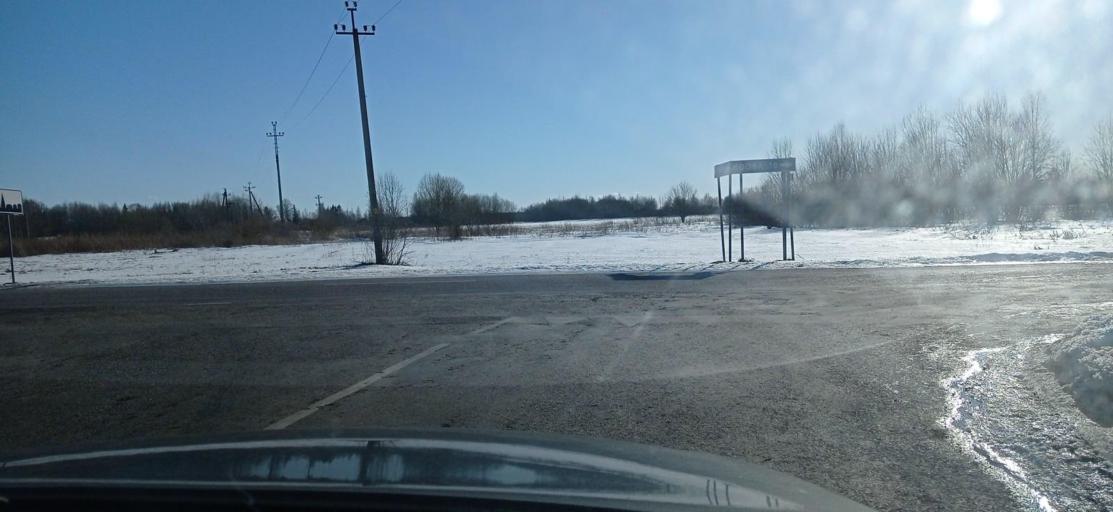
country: EE
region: Tartu
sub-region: Alatskivi vald
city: Kallaste
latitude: 58.4920
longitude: 27.2349
